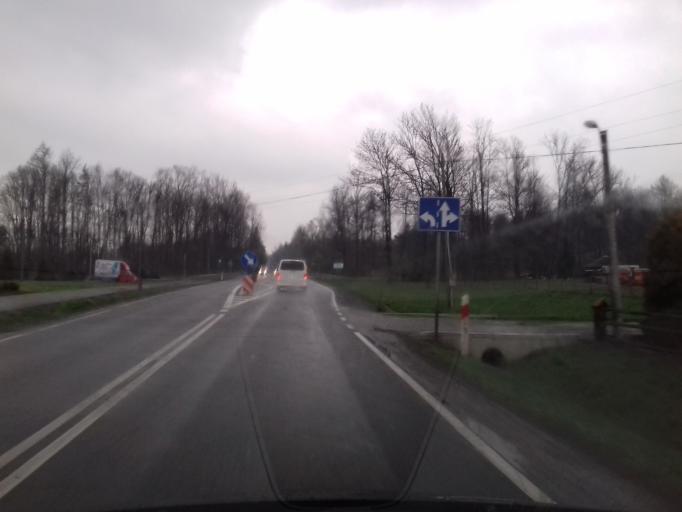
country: PL
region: Lesser Poland Voivodeship
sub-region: Powiat nowosadecki
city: Stary Sacz
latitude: 49.5597
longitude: 20.6554
